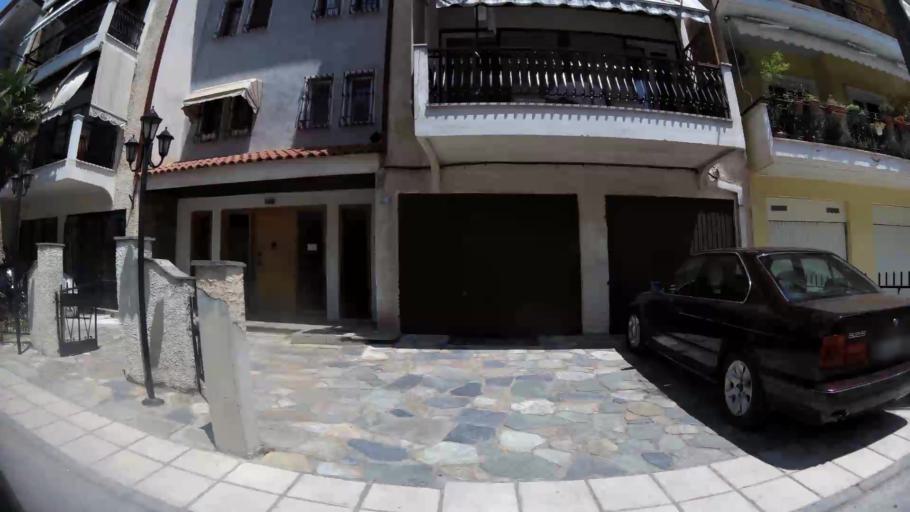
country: GR
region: Central Macedonia
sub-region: Nomos Imathias
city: Veroia
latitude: 40.5111
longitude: 22.2081
